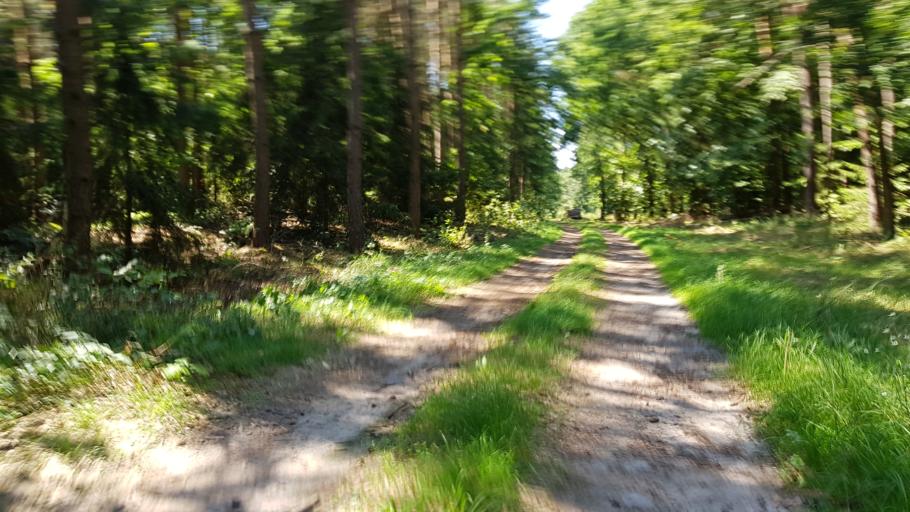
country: PL
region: West Pomeranian Voivodeship
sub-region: Powiat gryfinski
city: Banie
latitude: 53.1583
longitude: 14.6151
